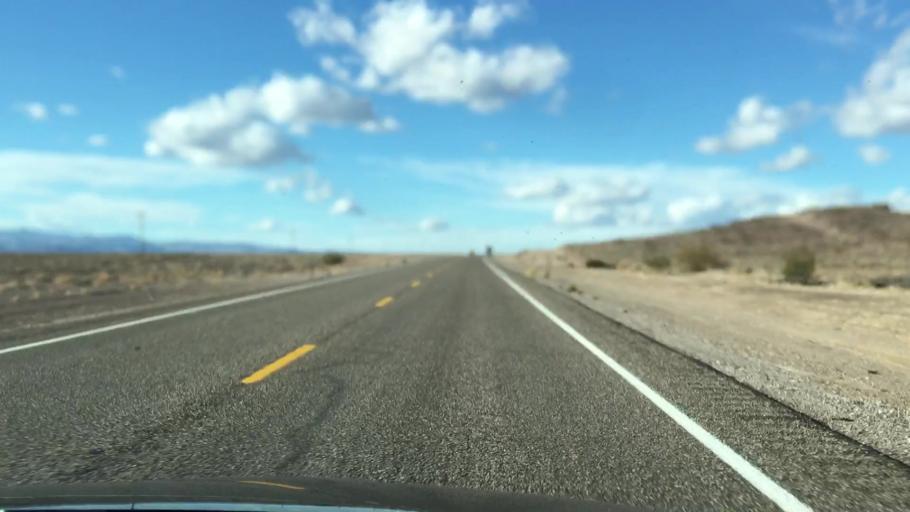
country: US
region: Nevada
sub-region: Nye County
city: Beatty
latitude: 37.1916
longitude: -116.9446
